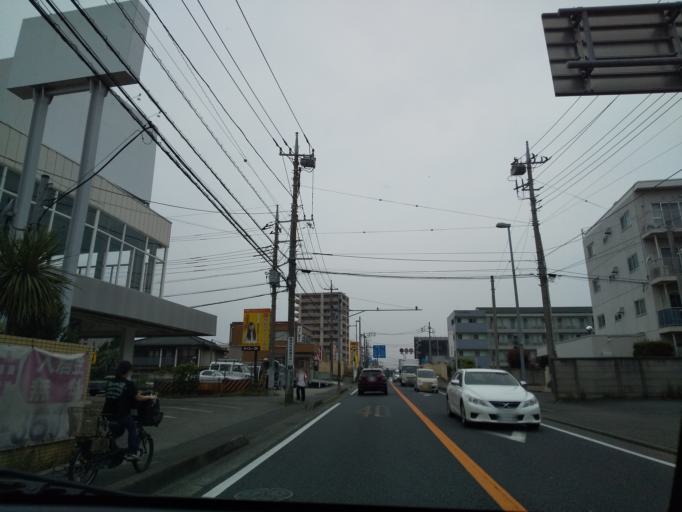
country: JP
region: Kanagawa
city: Zama
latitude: 35.5071
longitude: 139.4164
